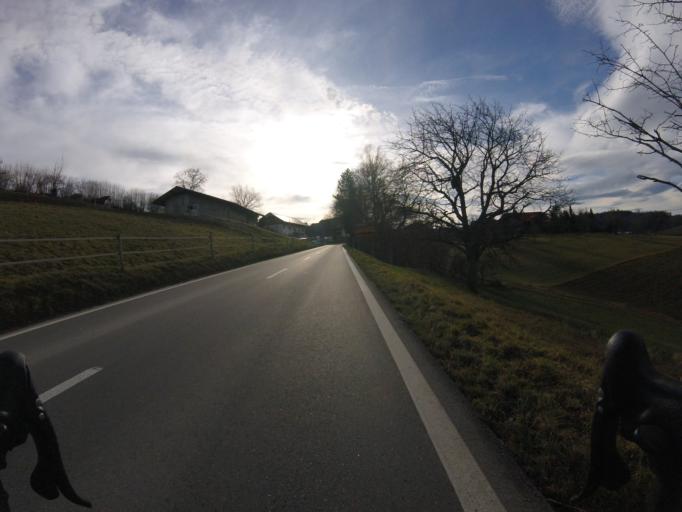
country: CH
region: Fribourg
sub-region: Sense District
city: Ueberstorf
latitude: 46.8589
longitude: 7.3154
